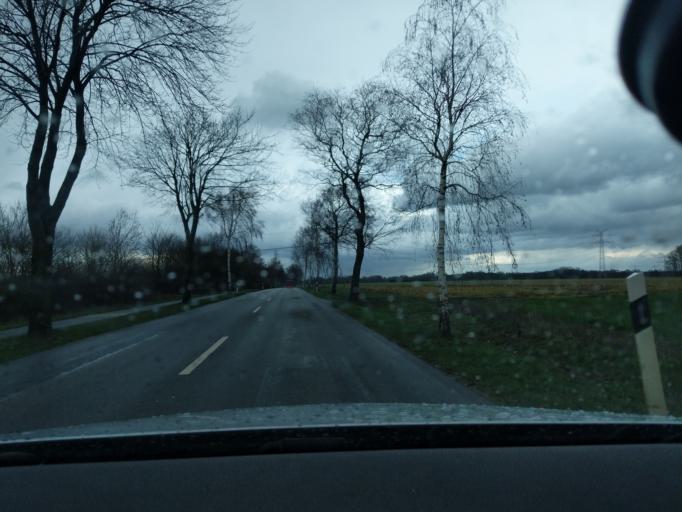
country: DE
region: Lower Saxony
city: Kutenholz
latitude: 53.5079
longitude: 9.3613
